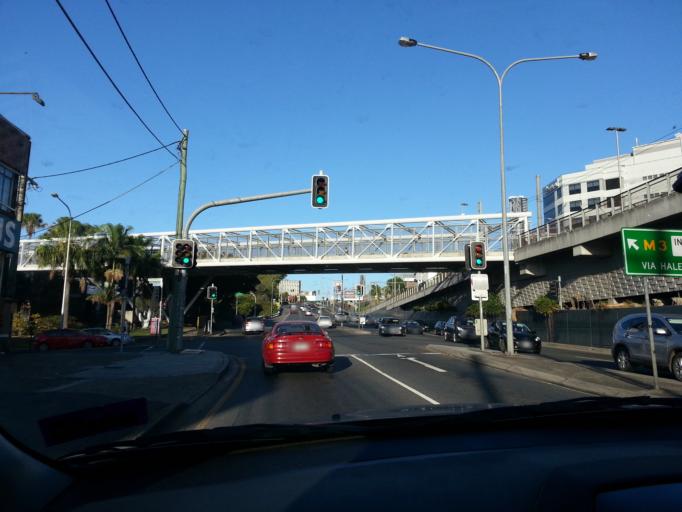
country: AU
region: Queensland
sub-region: Brisbane
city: Milton
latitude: -27.4674
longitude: 153.0086
